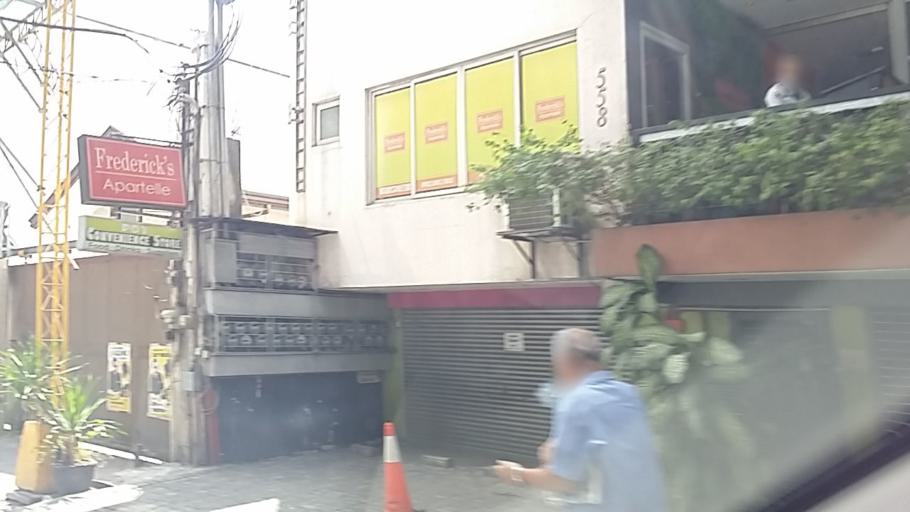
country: PH
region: Metro Manila
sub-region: Mandaluyong
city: Mandaluyong City
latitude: 14.5763
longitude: 121.0492
